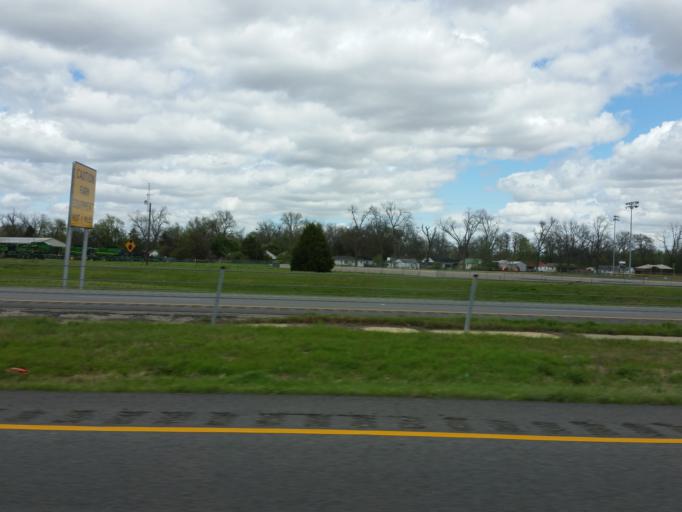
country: US
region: Arkansas
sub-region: Poinsett County
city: Marked Tree
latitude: 35.5256
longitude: -90.4296
